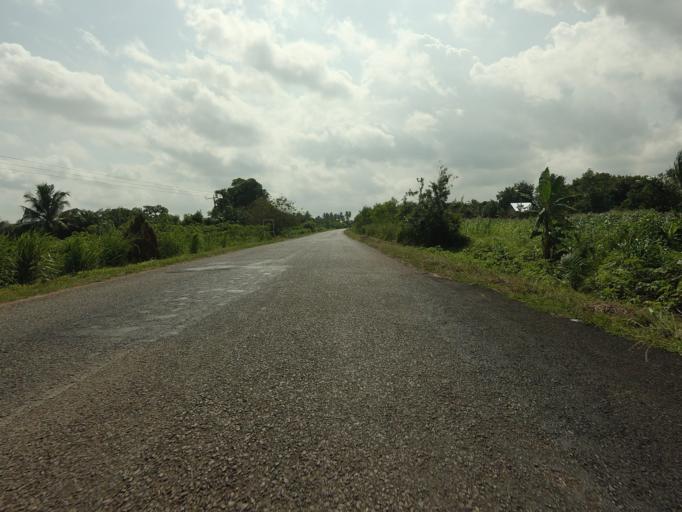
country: GH
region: Volta
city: Ho
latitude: 6.4115
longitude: 0.7609
